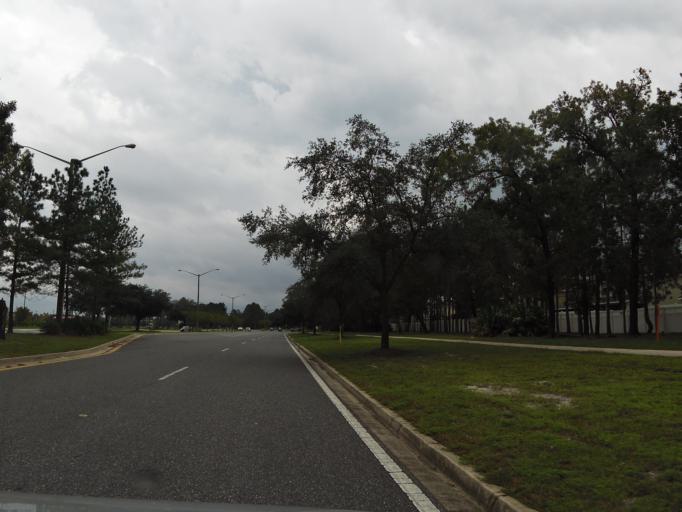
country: US
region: Florida
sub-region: Clay County
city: Lakeside
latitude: 30.1619
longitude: -81.8402
